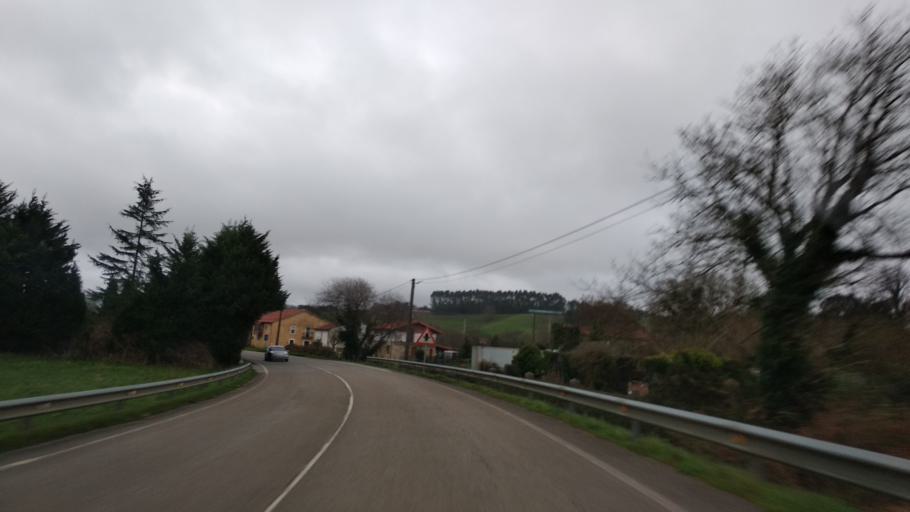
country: ES
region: Cantabria
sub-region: Provincia de Cantabria
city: Entrambasaguas
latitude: 43.4044
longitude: -3.7186
